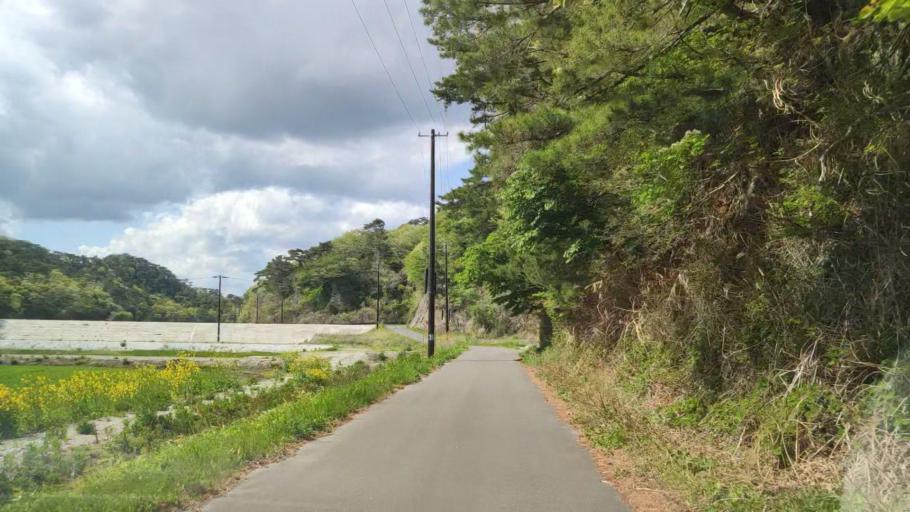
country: JP
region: Miyagi
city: Yamoto
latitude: 38.3396
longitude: 141.1643
